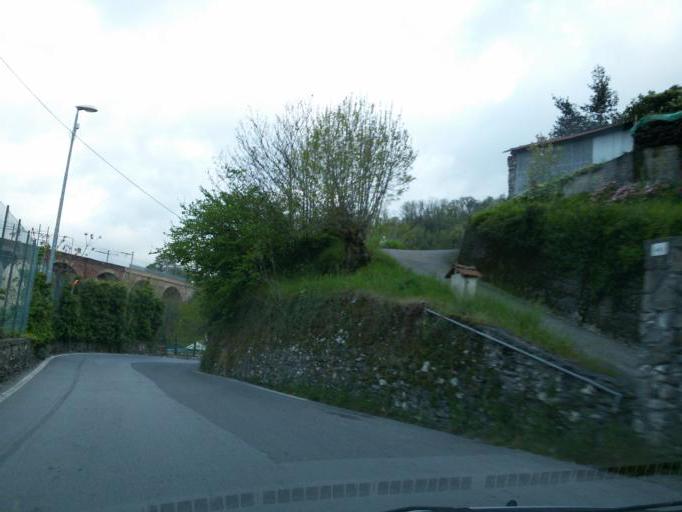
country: IT
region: Liguria
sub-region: Provincia di Genova
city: Santa Marta
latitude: 44.4737
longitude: 8.8909
